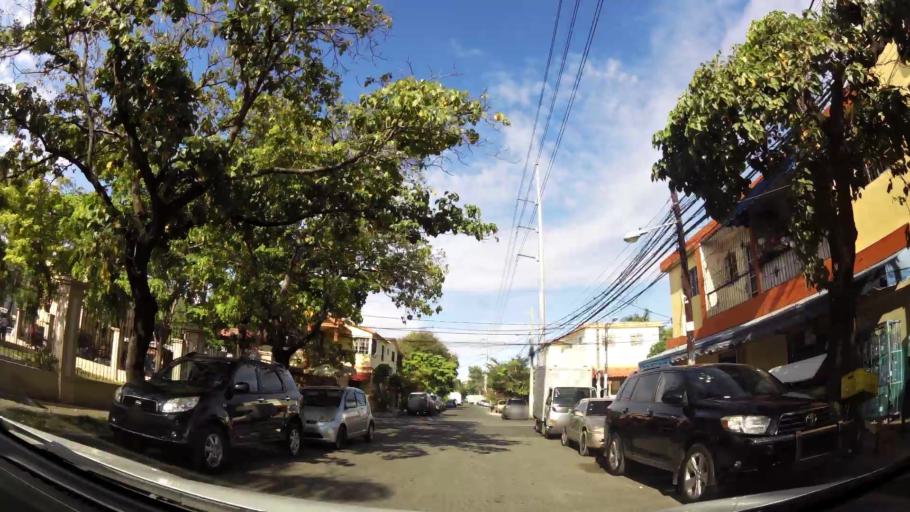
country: DO
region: Santo Domingo
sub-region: Santo Domingo
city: Santo Domingo Este
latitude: 18.4868
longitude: -69.8754
